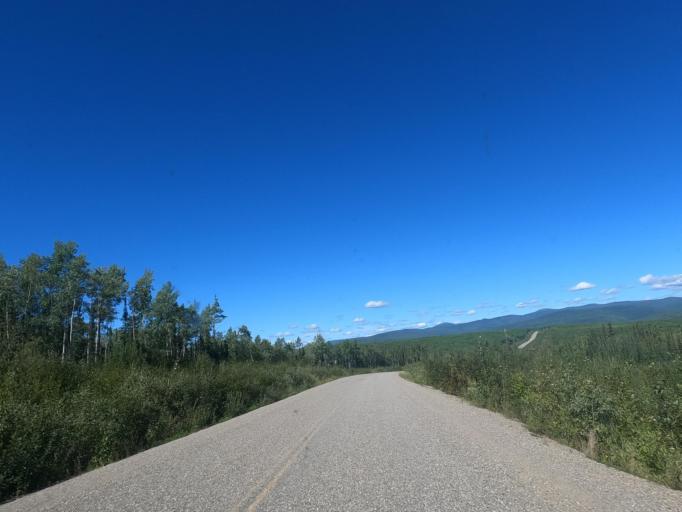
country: CA
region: Yukon
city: Dawson City
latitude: 63.7353
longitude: -137.6785
